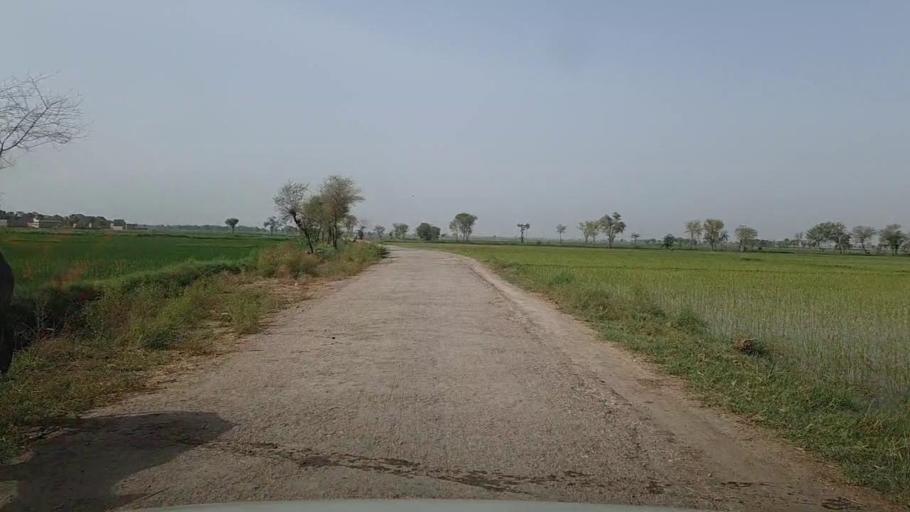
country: PK
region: Sindh
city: Mehar
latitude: 27.1159
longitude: 67.8197
